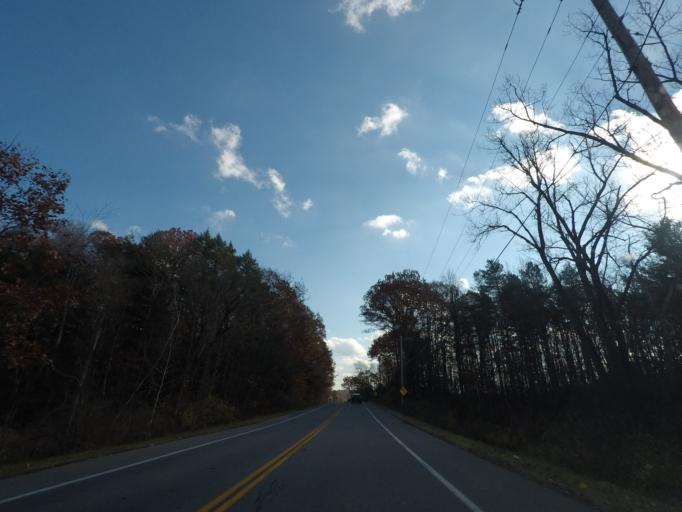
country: US
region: New York
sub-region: Schenectady County
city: East Glenville
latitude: 42.8993
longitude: -73.8945
